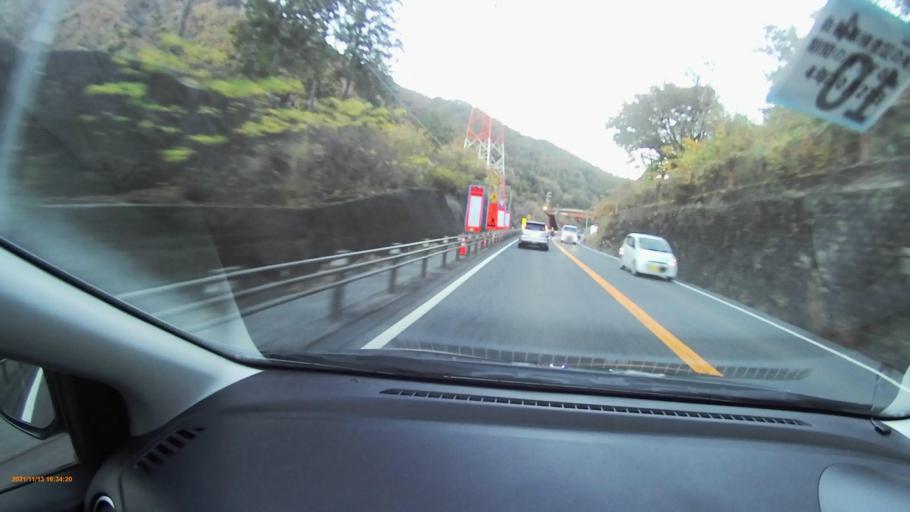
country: JP
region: Gifu
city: Nakatsugawa
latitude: 35.5923
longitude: 137.5983
